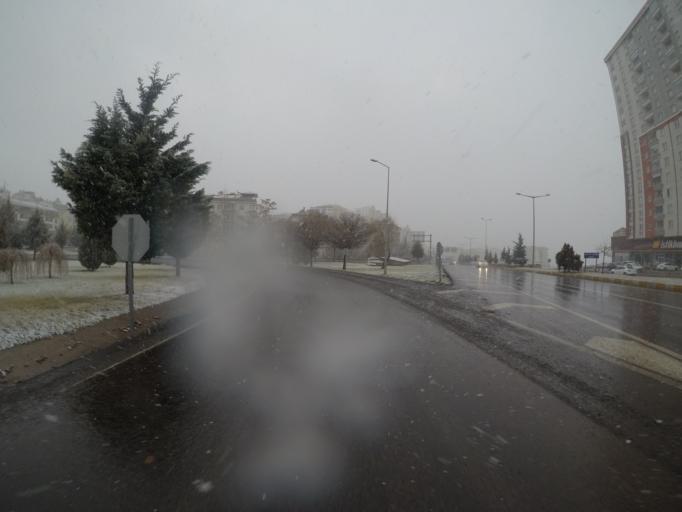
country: TR
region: Nevsehir
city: Nevsehir
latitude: 38.6307
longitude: 34.7284
